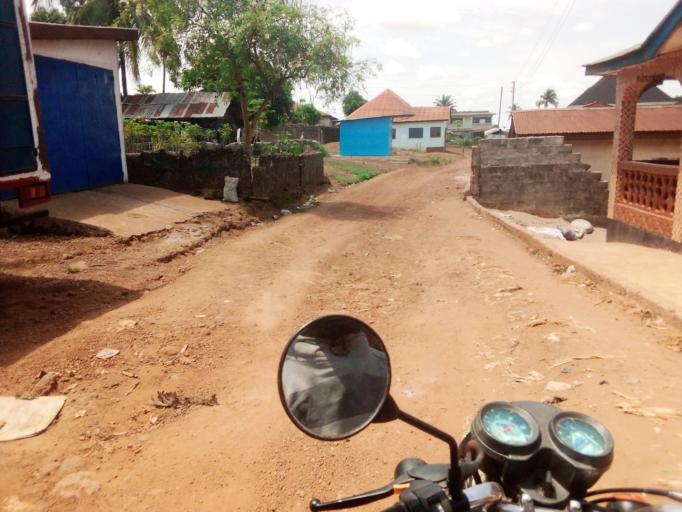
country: SL
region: Western Area
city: Waterloo
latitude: 8.3318
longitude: -13.0746
